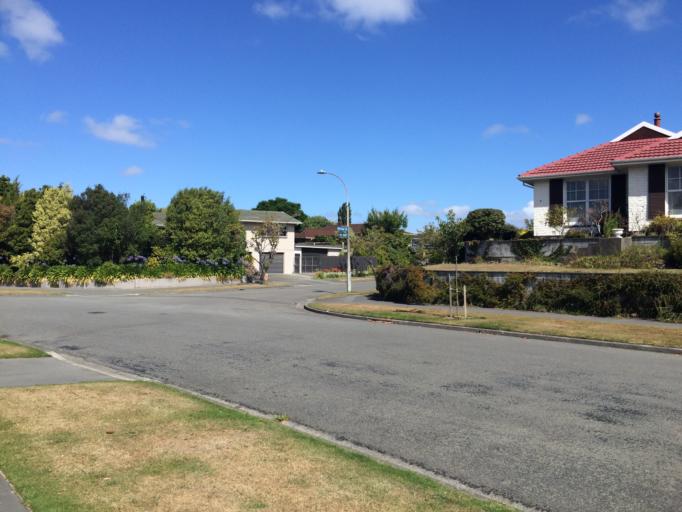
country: NZ
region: Canterbury
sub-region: Selwyn District
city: Prebbleton
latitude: -43.5222
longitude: 172.5554
